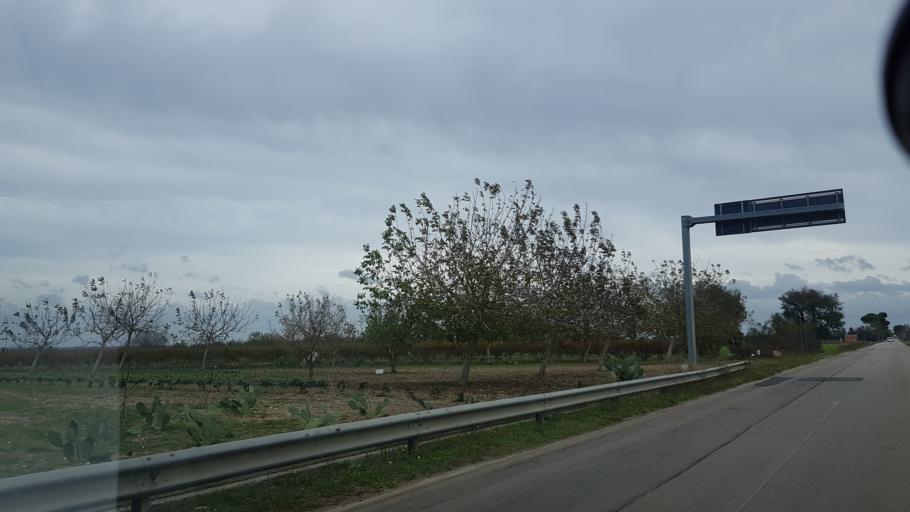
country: IT
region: Apulia
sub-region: Provincia di Brindisi
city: San Pancrazio Salentino
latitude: 40.4153
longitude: 17.8507
